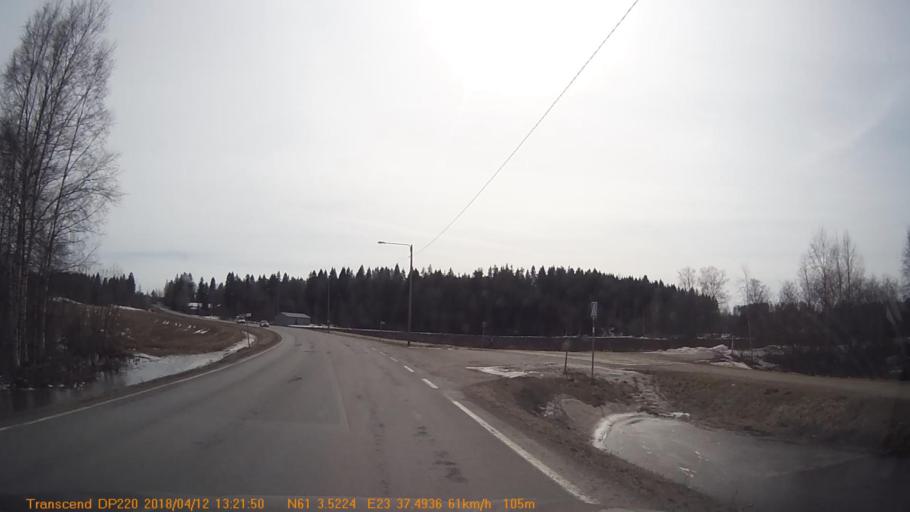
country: FI
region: Pirkanmaa
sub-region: Etelae-Pirkanmaa
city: Urjala
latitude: 61.0578
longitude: 23.6249
